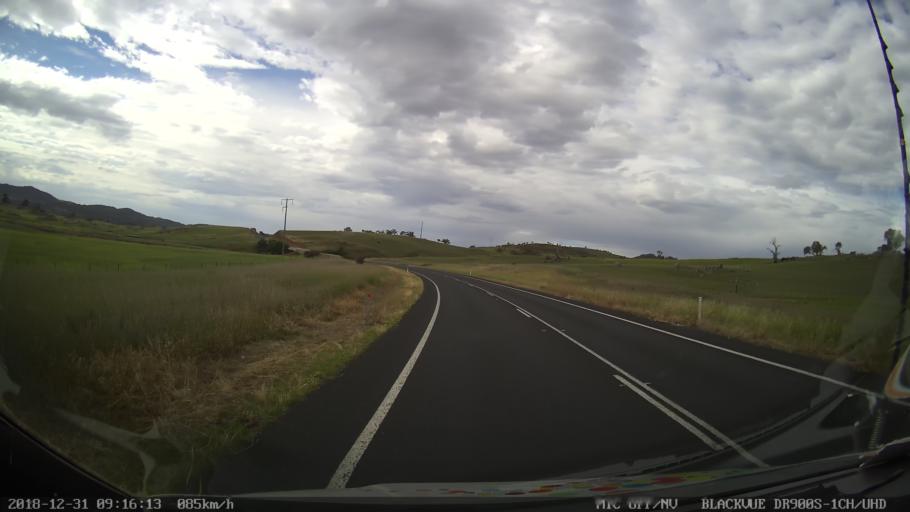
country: AU
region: New South Wales
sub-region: Snowy River
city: Jindabyne
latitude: -36.3936
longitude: 148.5941
